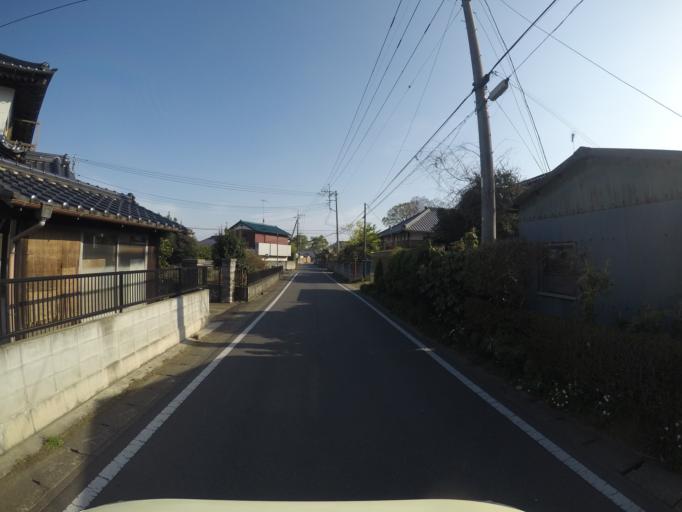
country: JP
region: Ibaraki
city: Ishige
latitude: 36.1696
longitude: 140.0168
